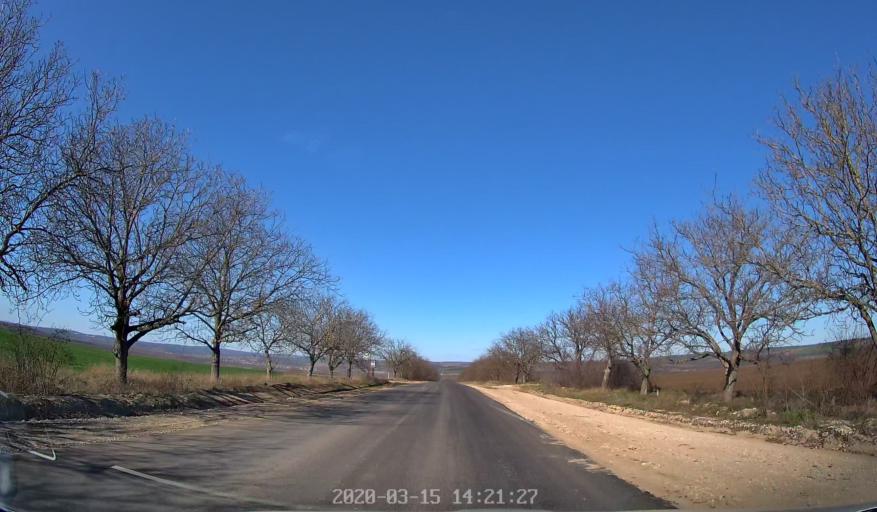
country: MD
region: Orhei
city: Orhei
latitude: 47.3181
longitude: 28.9253
